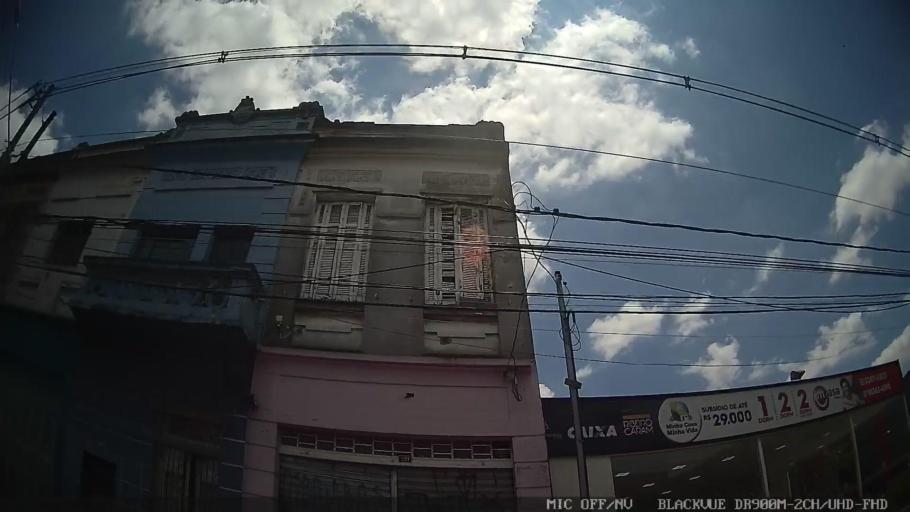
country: BR
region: Sao Paulo
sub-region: Sao Paulo
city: Sao Paulo
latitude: -23.5540
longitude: -46.6207
